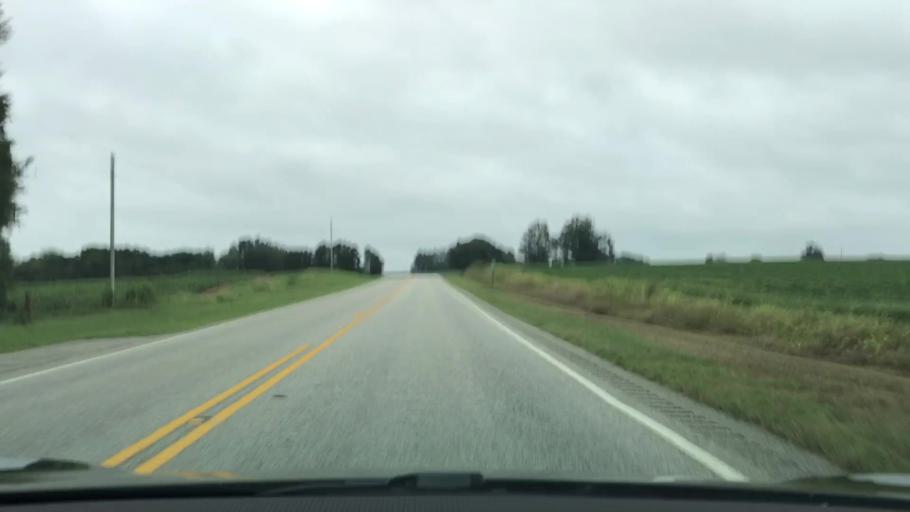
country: US
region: Alabama
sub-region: Coffee County
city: Elba
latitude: 31.3167
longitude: -86.1343
